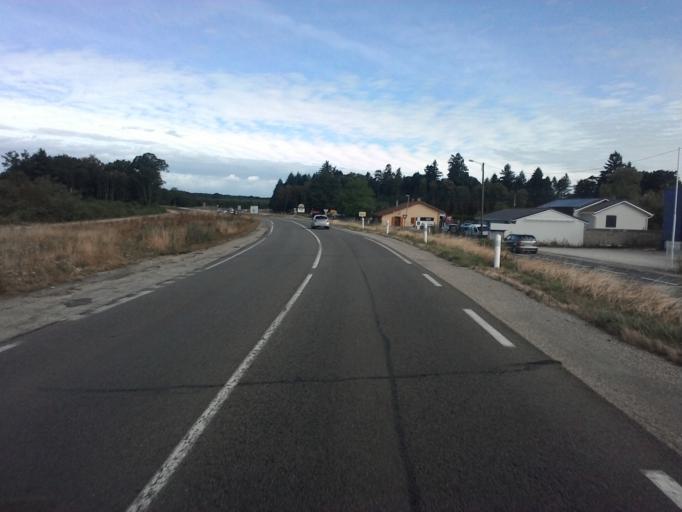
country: FR
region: Rhone-Alpes
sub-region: Departement de l'Ain
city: Montagnat
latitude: 46.1634
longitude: 5.2684
